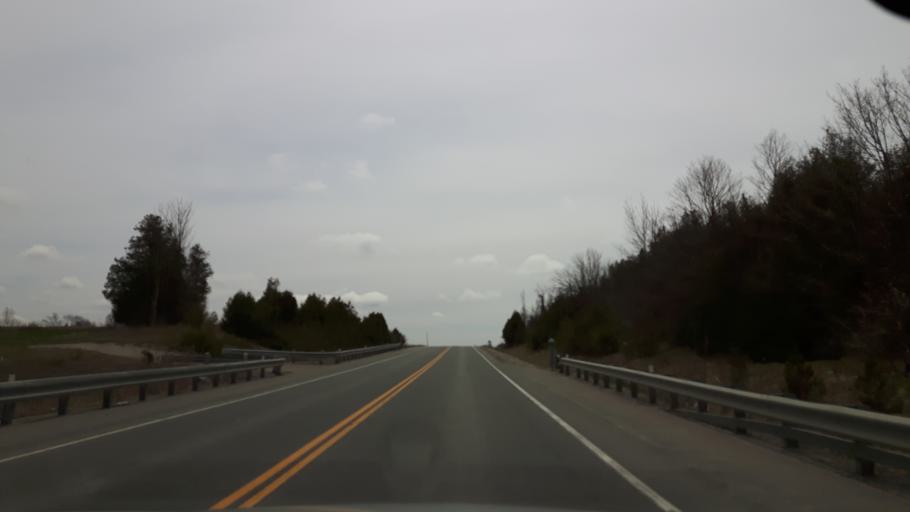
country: CA
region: Ontario
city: Goderich
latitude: 43.6138
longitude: -81.7057
